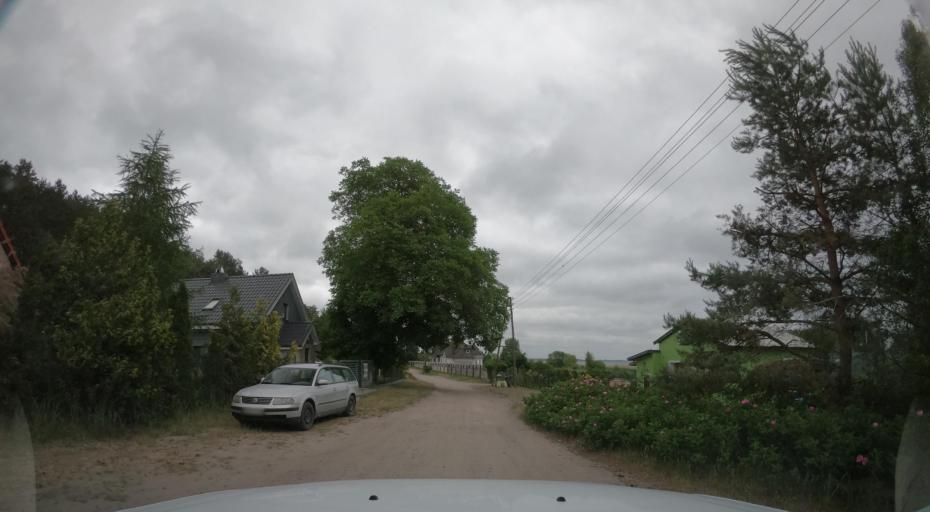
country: PL
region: West Pomeranian Voivodeship
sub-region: Powiat kamienski
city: Wolin
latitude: 53.8599
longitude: 14.5210
